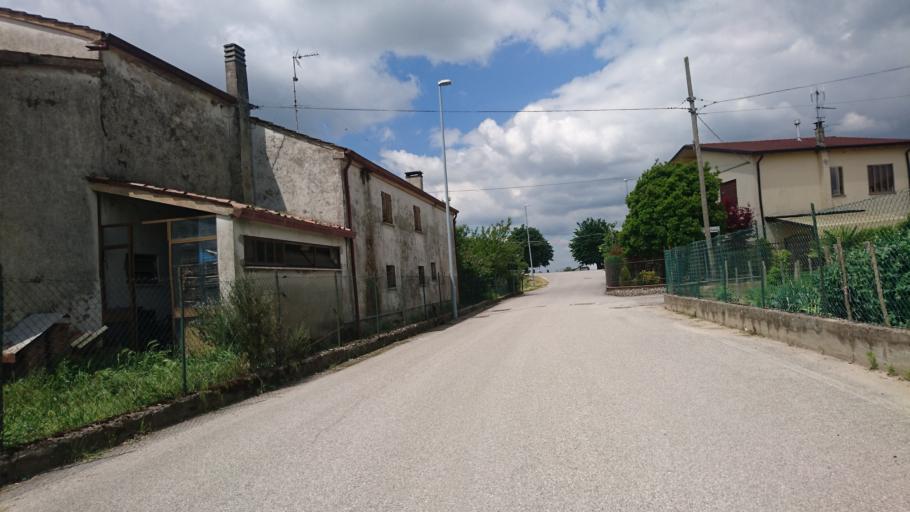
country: IT
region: Veneto
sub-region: Provincia di Padova
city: Vighizzolo d'Este
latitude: 45.1451
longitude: 11.6456
